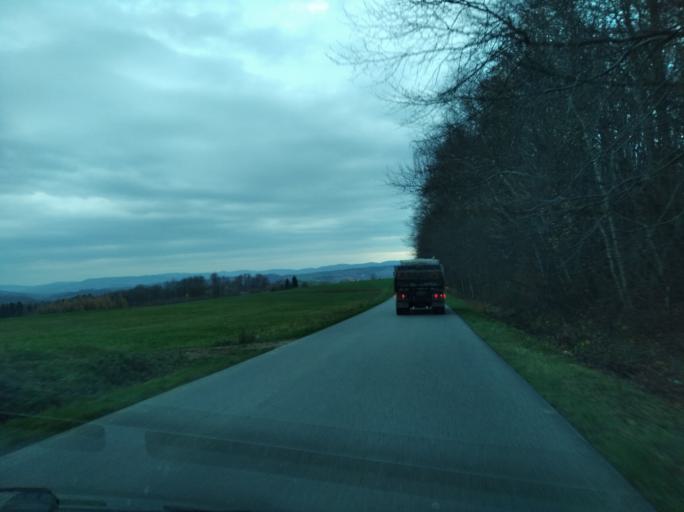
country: PL
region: Subcarpathian Voivodeship
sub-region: Powiat ropczycko-sedziszowski
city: Zagorzyce
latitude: 49.9446
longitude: 21.6937
